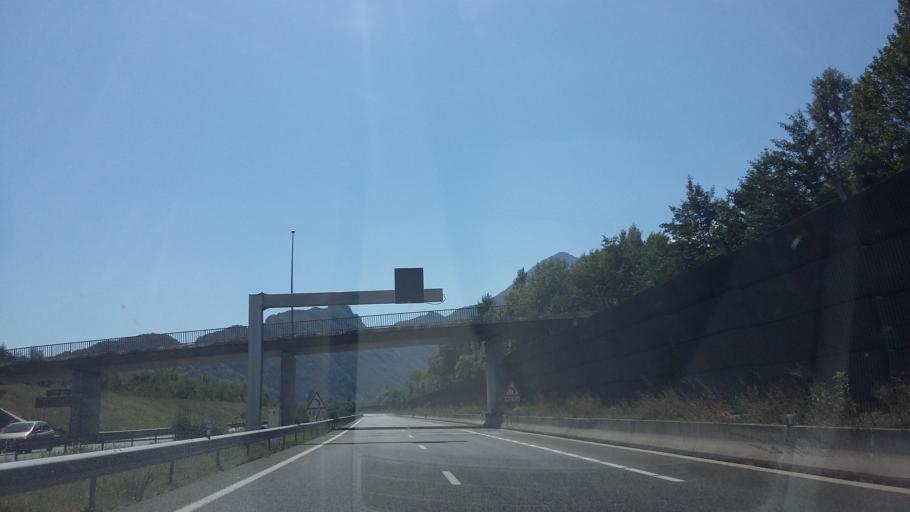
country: FR
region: Rhone-Alpes
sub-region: Departement de l'Isere
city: Allieres-et-Risset
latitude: 45.0943
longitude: 5.6700
